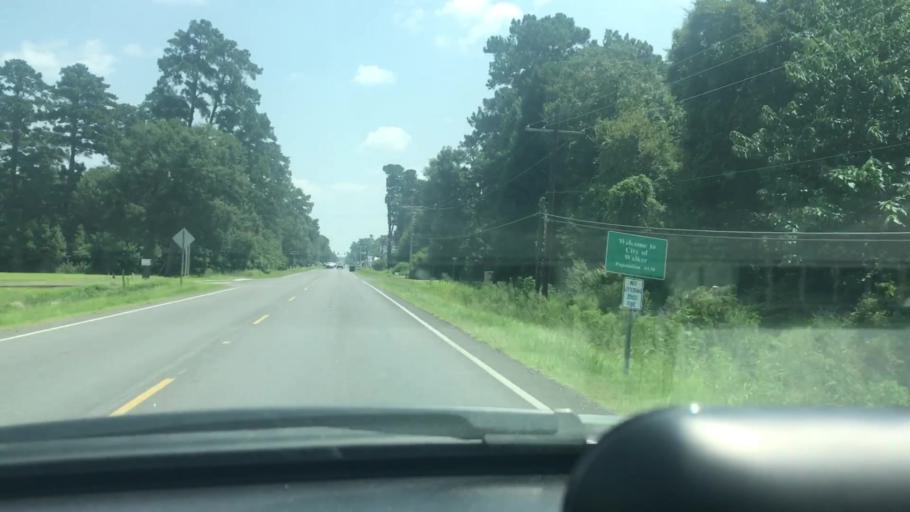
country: US
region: Louisiana
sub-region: Livingston Parish
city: Walker
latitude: 30.4851
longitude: -90.8922
